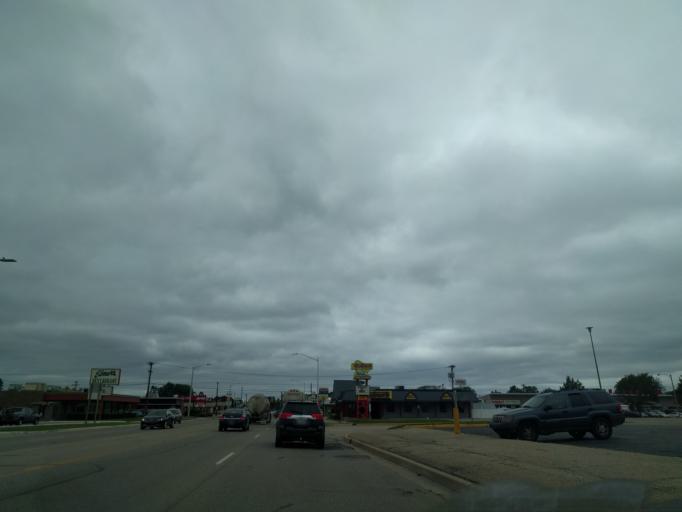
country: US
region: Michigan
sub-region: Delta County
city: Escanaba
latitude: 45.7478
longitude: -87.0798
